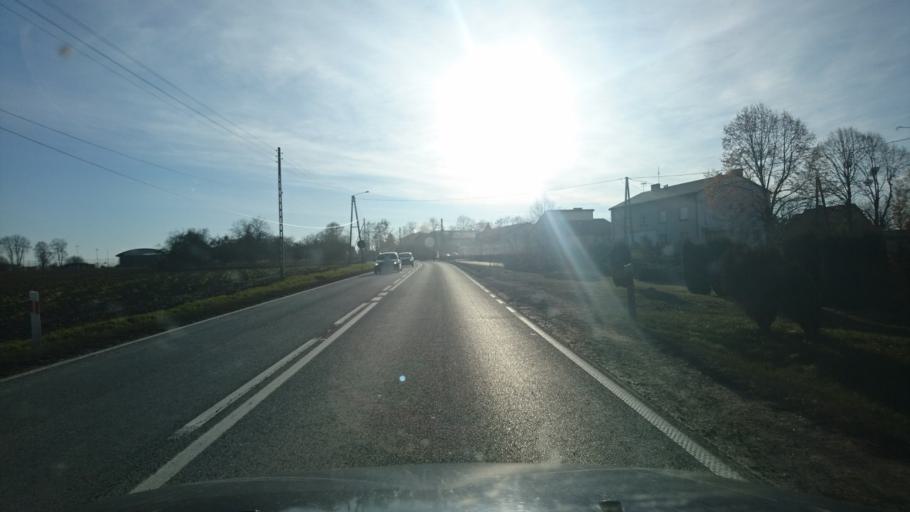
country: PL
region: Opole Voivodeship
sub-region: Powiat oleski
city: Dalachow
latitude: 51.0445
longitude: 18.5968
